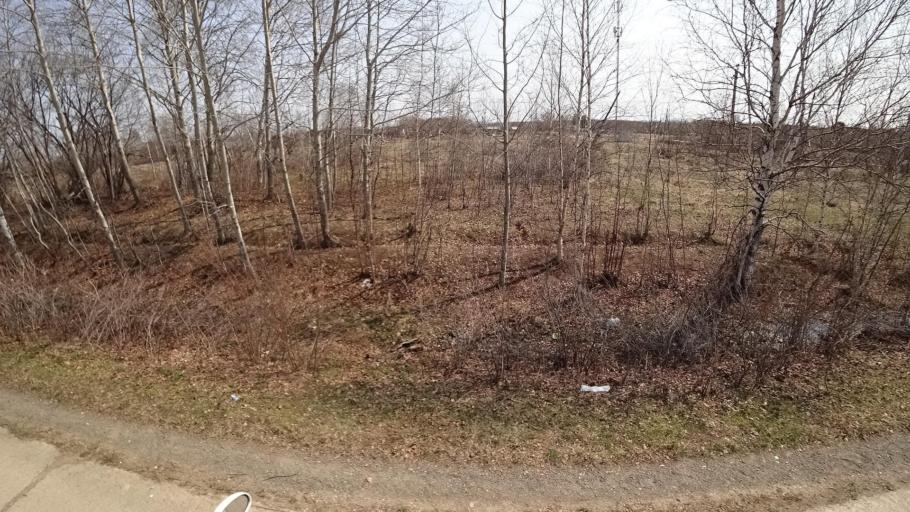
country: RU
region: Khabarovsk Krai
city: Selikhino
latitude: 50.3852
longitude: 137.3733
